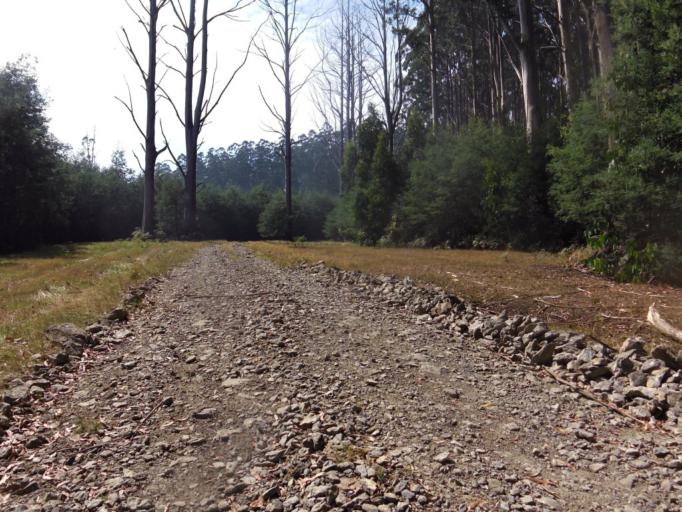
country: AU
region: Victoria
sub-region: Yarra Ranges
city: Healesville
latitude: -37.5659
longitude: 145.5979
